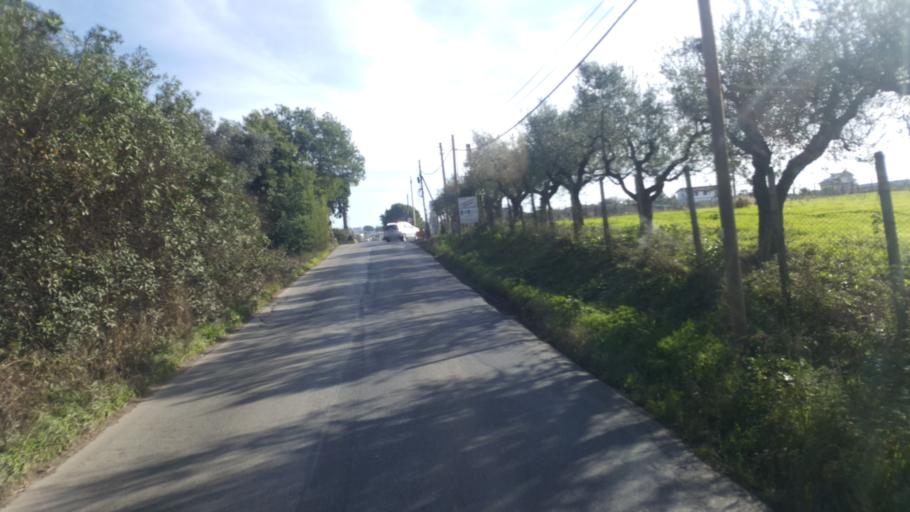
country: IT
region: Latium
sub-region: Citta metropolitana di Roma Capitale
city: Mantiglia di Ardea
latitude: 41.6815
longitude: 12.6188
